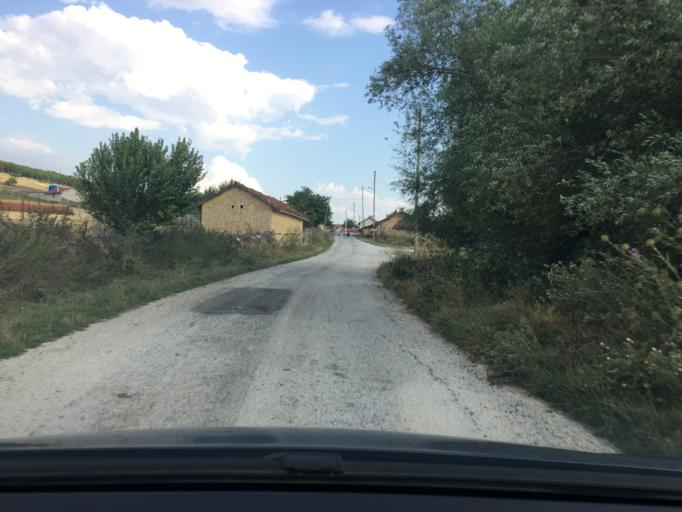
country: TR
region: Eskisehir
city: Kirka
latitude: 39.2792
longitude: 30.6746
